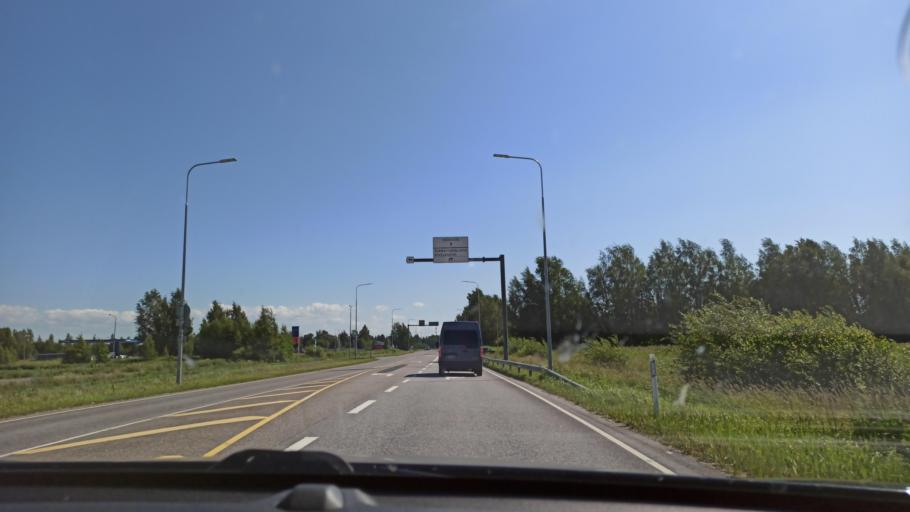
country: FI
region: Satakunta
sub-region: Pori
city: Pori
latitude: 61.5139
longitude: 21.8032
